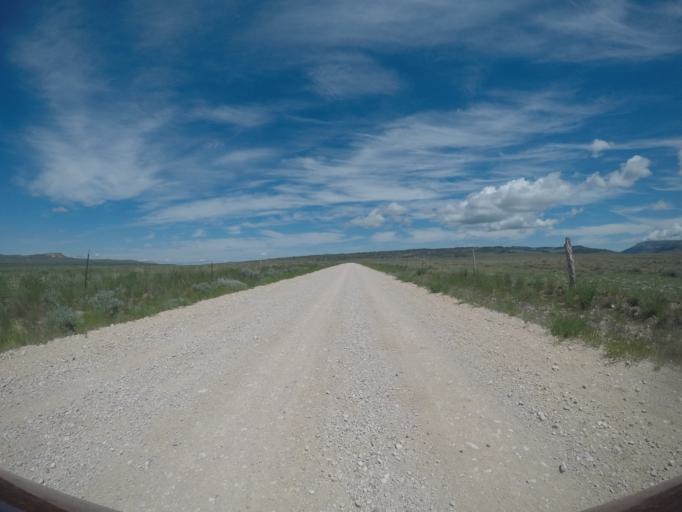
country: US
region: Montana
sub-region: Yellowstone County
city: Laurel
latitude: 45.2255
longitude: -108.6995
